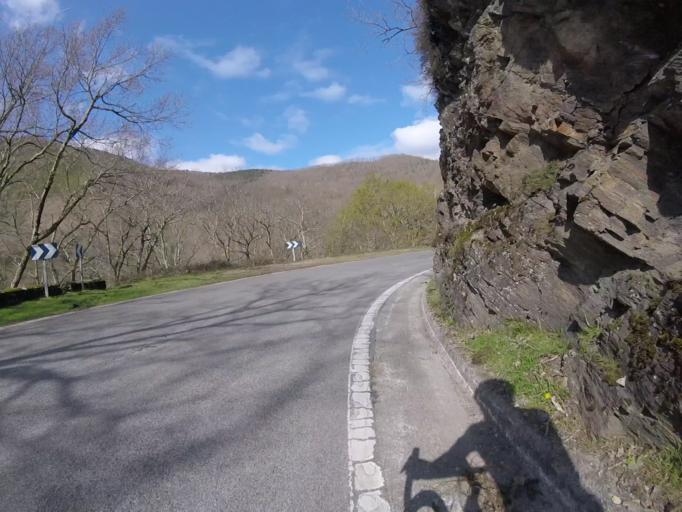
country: ES
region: Navarre
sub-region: Provincia de Navarra
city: Goizueta
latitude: 43.1469
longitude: -1.8531
